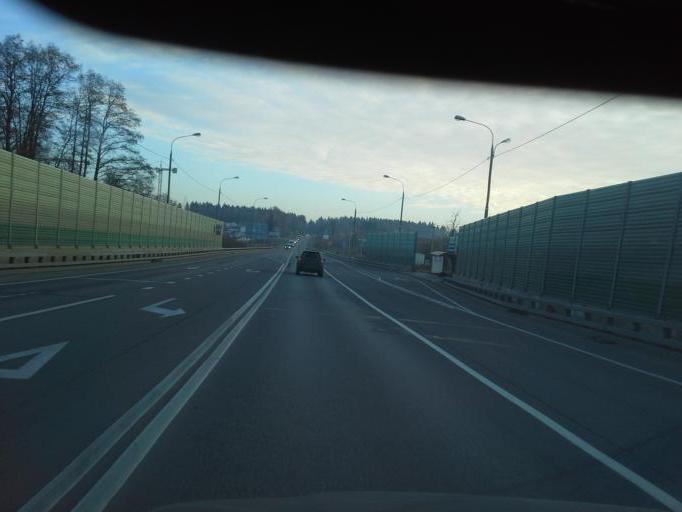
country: RU
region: Moskovskaya
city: Zhavoronki
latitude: 55.6122
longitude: 37.1005
